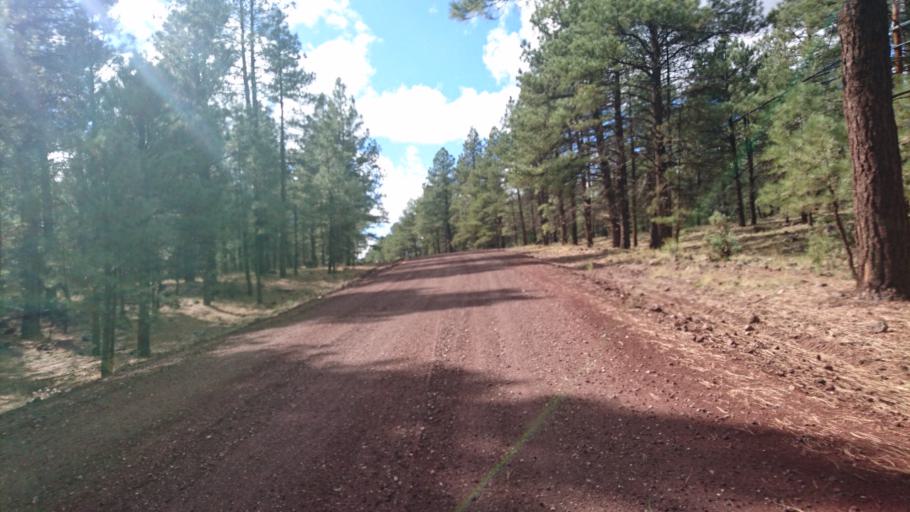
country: US
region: Arizona
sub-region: Coconino County
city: Williams
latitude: 35.2623
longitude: -112.1033
